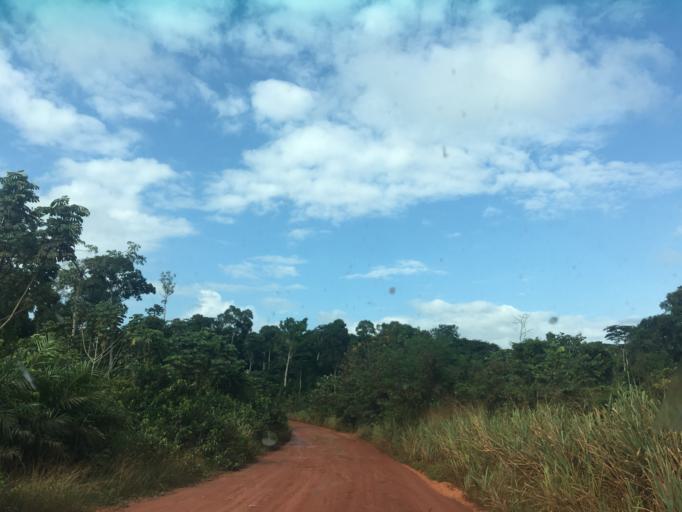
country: GH
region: Western
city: Wassa-Akropong
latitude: 5.9613
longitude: -2.4266
